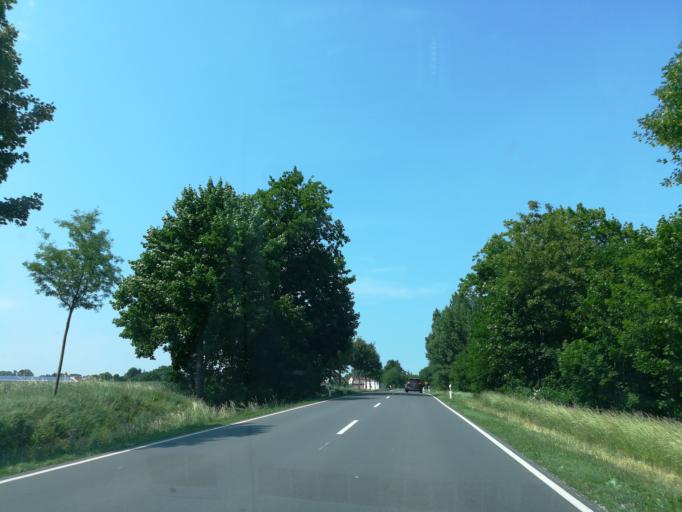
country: DE
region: Saxony-Anhalt
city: Aschersleben
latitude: 51.8161
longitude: 11.4569
